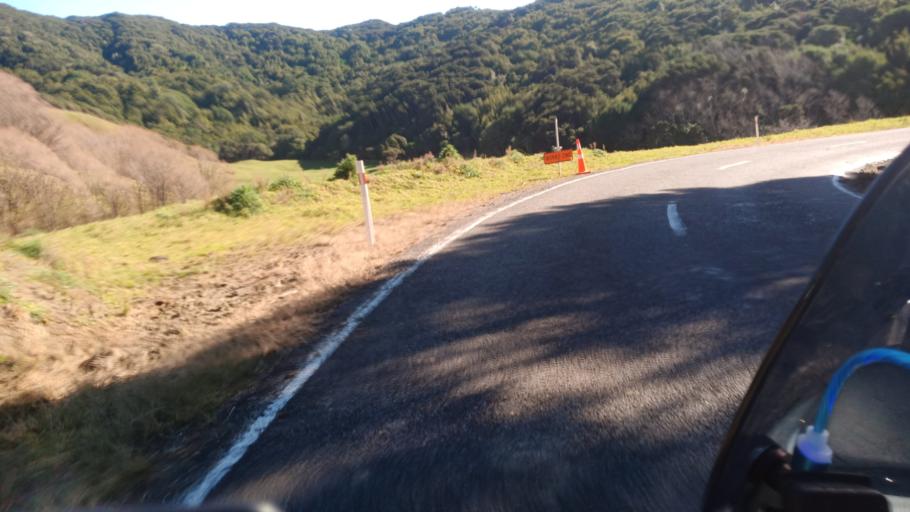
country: NZ
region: Gisborne
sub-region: Gisborne District
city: Gisborne
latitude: -38.2497
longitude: 178.3103
